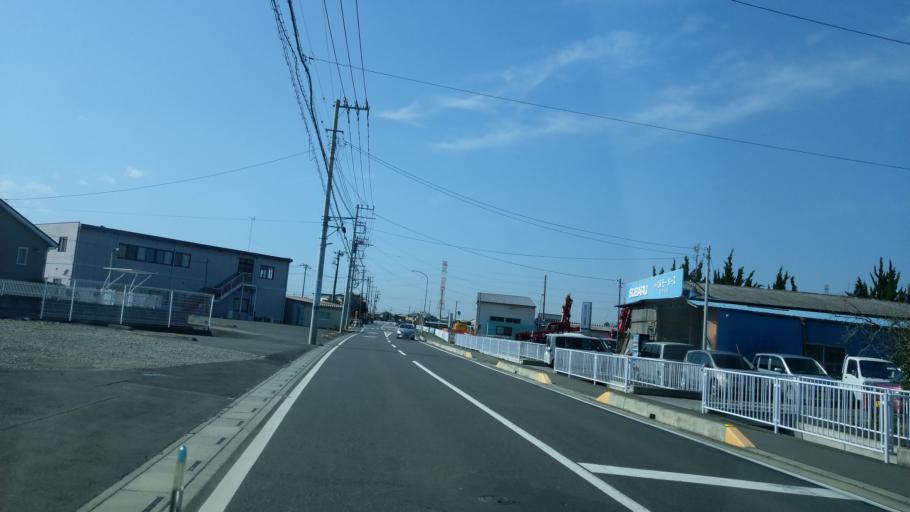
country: JP
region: Saitama
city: Kawagoe
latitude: 35.9814
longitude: 139.4829
